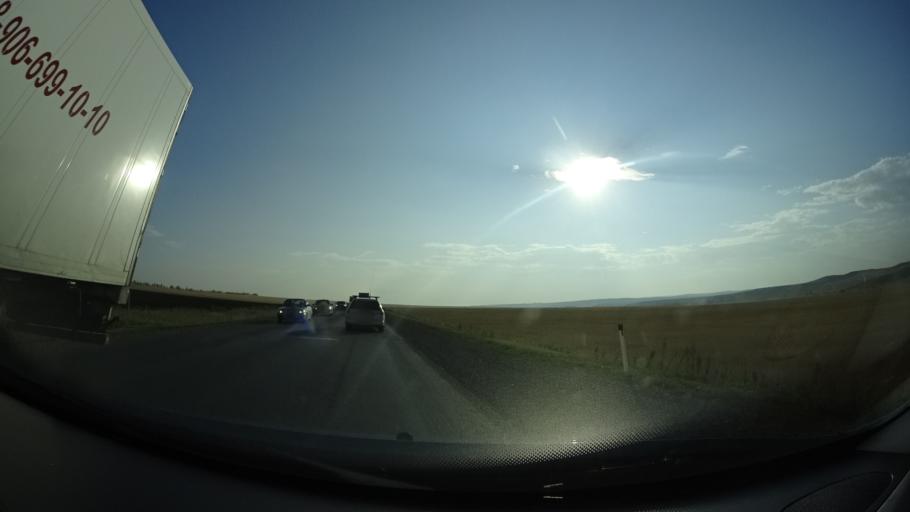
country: RU
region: Orenburg
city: Severnoye
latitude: 54.1261
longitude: 52.5659
